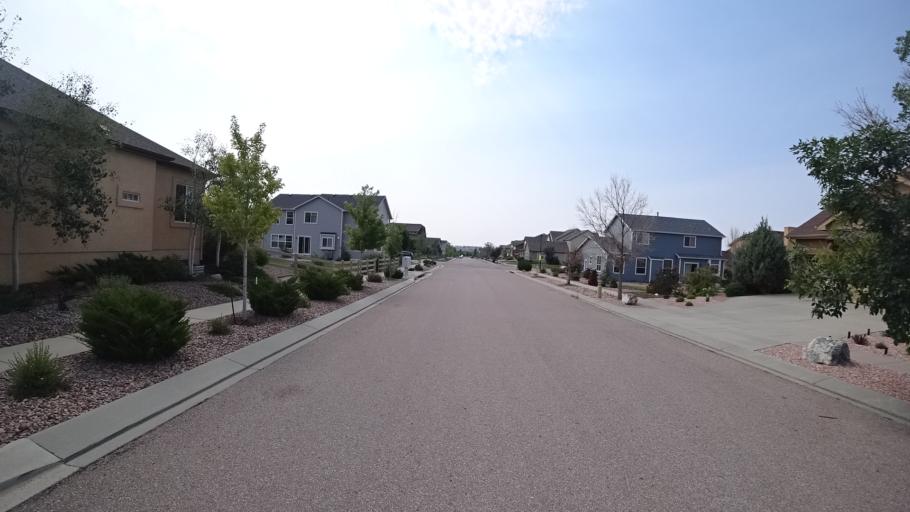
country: US
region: Colorado
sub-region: El Paso County
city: Black Forest
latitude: 38.9645
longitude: -104.7219
